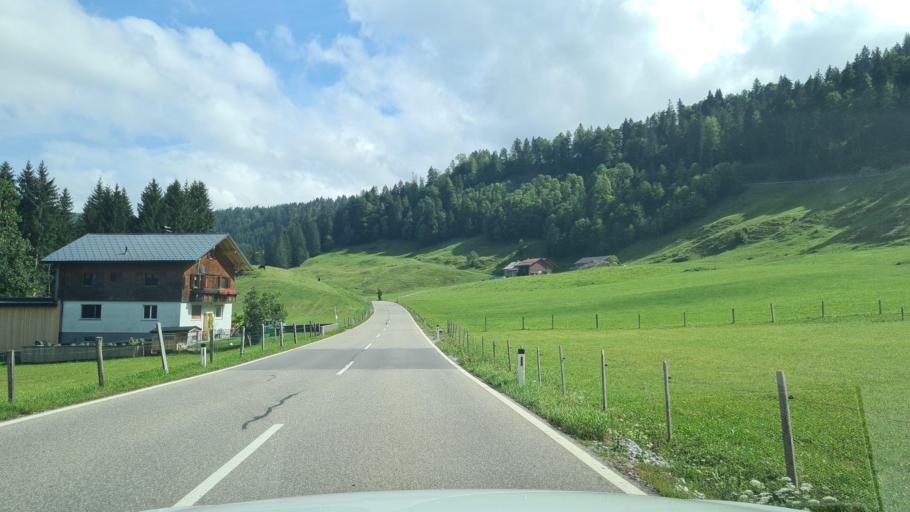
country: AT
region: Vorarlberg
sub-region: Politischer Bezirk Bregenz
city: Sibratsgfall
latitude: 47.4509
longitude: 10.0032
